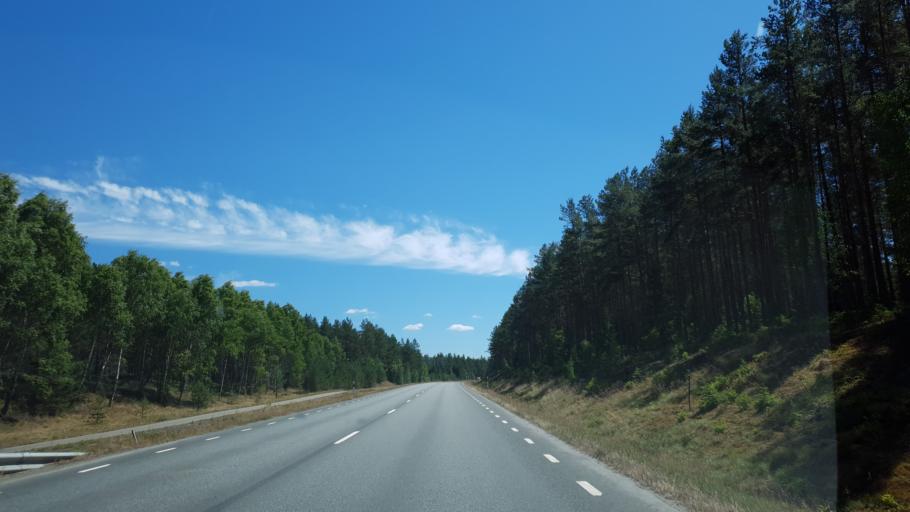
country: SE
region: Joenkoeping
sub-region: Vaggeryds Kommun
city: Vaggeryd
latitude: 57.5268
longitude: 14.1247
